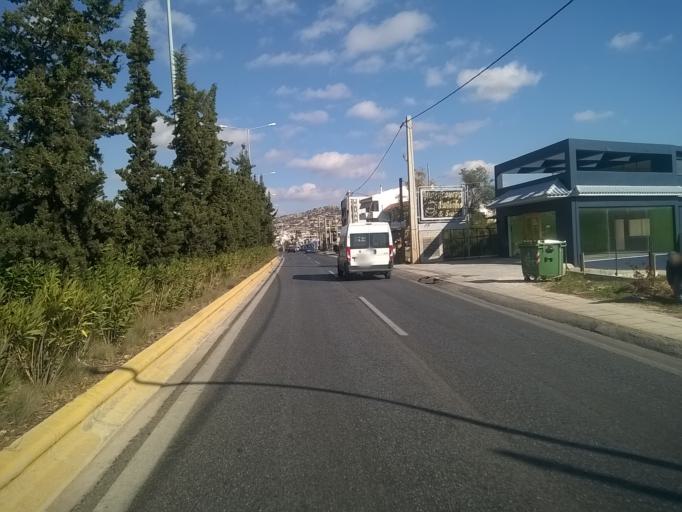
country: GR
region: Attica
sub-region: Nomarchia Anatolikis Attikis
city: Vari
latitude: 37.8423
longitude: 23.8176
